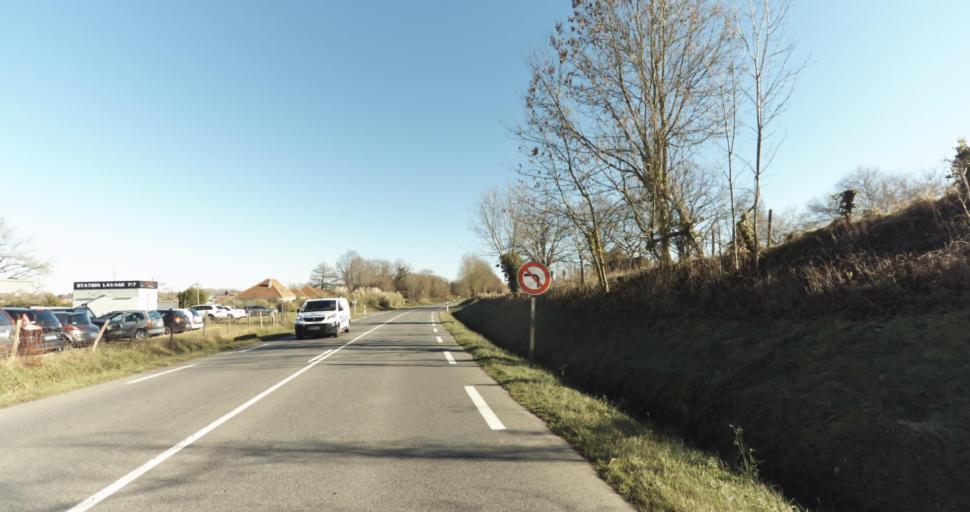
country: FR
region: Aquitaine
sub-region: Departement des Pyrenees-Atlantiques
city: Morlaas
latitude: 43.3383
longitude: -0.2633
